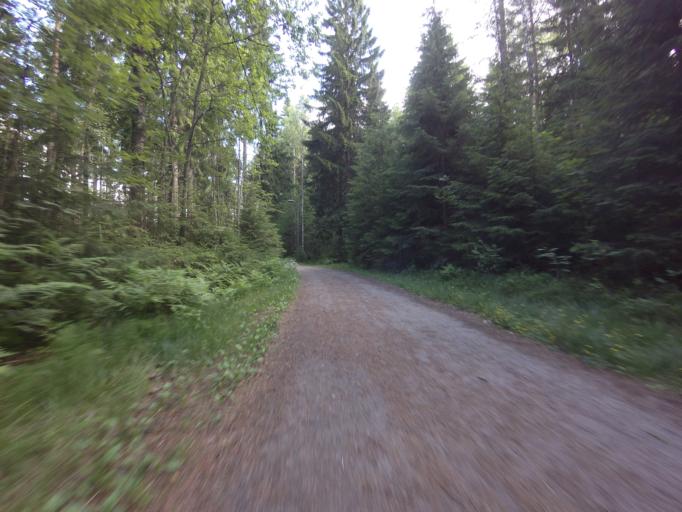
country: FI
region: Uusimaa
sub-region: Helsinki
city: Espoo
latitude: 60.1815
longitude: 24.6326
